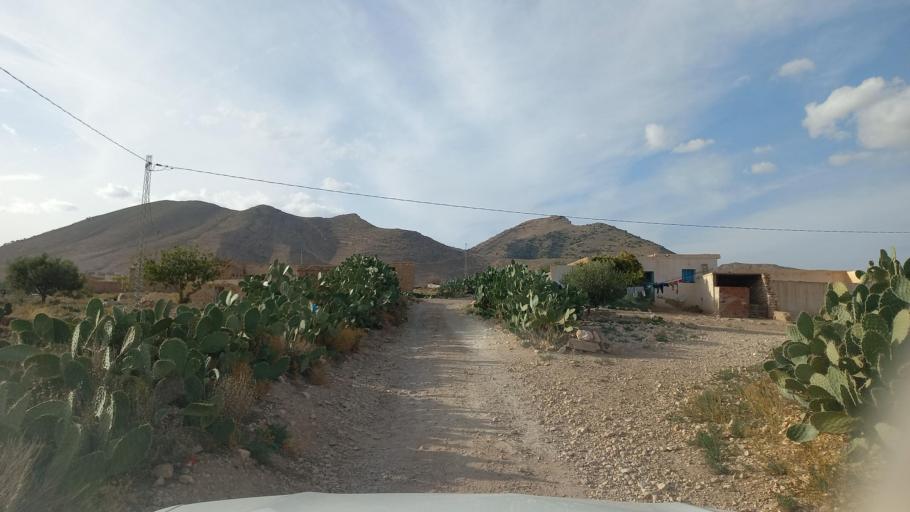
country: TN
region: Al Qasrayn
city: Sbiba
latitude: 35.4548
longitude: 9.0796
